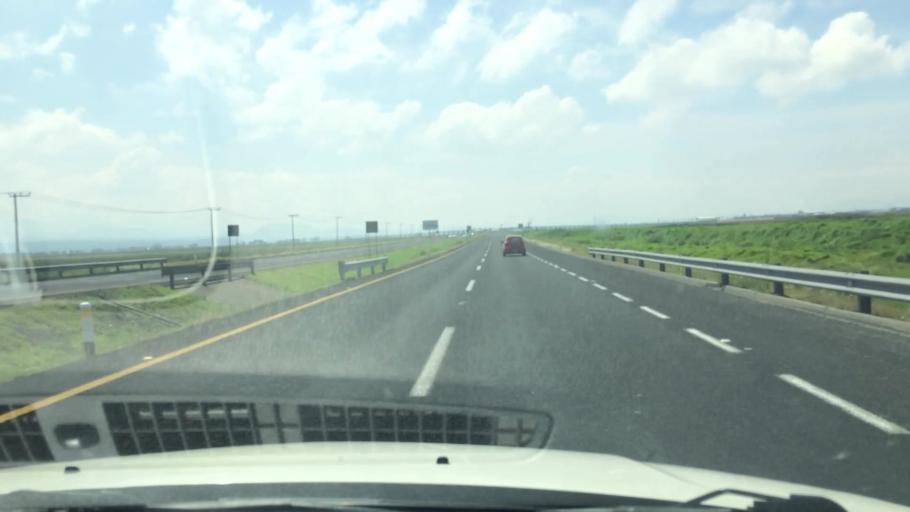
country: MX
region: Mexico
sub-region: Toluca
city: El Cerrillo Vista Hermosa
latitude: 19.3401
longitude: -99.5289
